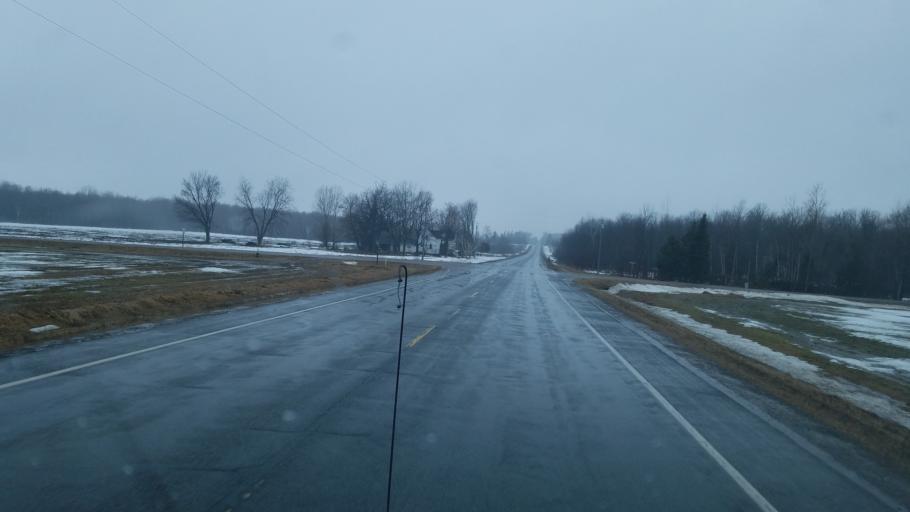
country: US
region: Wisconsin
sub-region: Marathon County
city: Spencer
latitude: 44.6777
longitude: -90.2779
